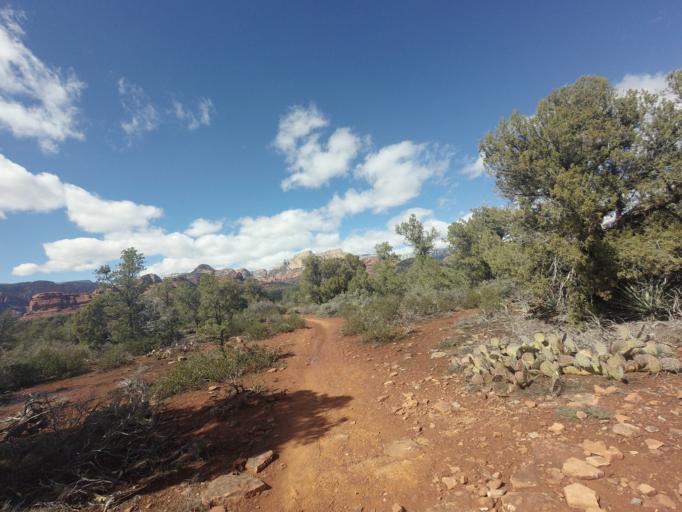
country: US
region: Arizona
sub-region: Yavapai County
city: West Sedona
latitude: 34.8976
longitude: -111.8222
